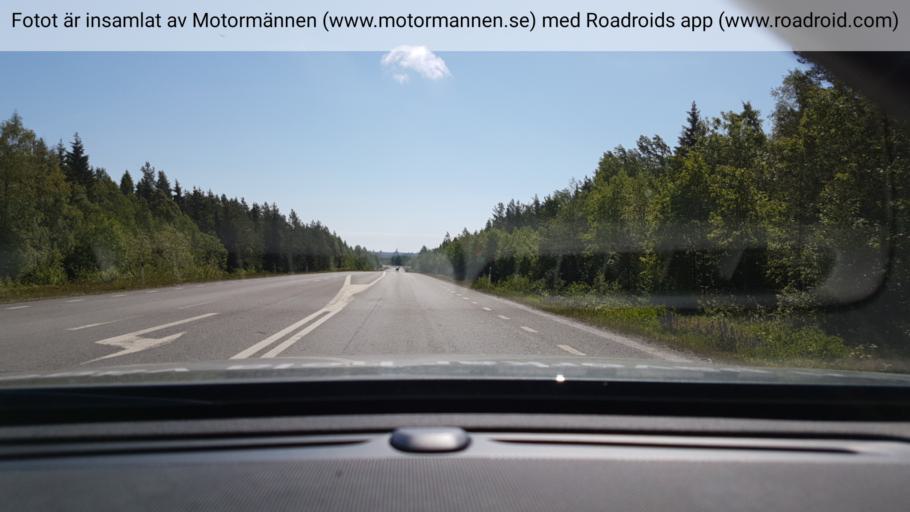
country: SE
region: Vaesterbotten
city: Obbola
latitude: 63.7140
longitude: 20.3100
